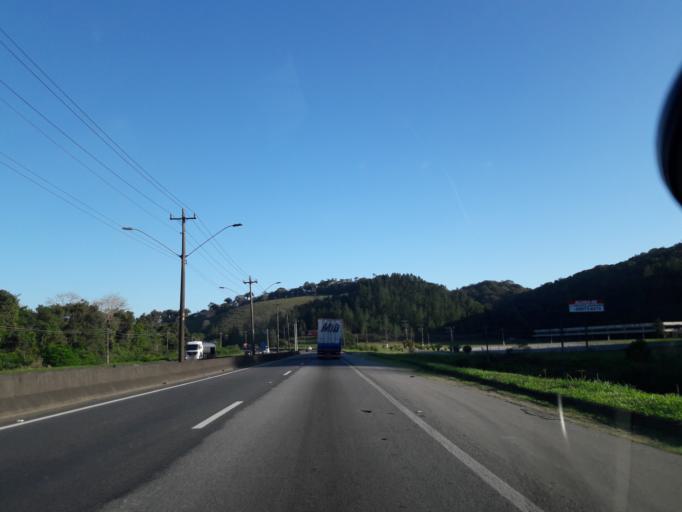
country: BR
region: Sao Paulo
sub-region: Sao Lourenco Da Serra
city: Sao Lourenco da Serra
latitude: -23.9084
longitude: -46.9918
